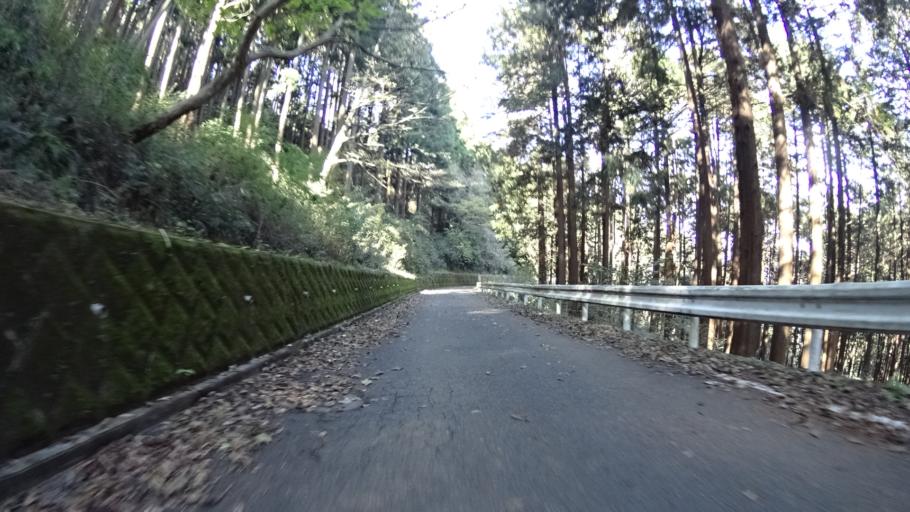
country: JP
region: Kanagawa
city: Atsugi
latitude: 35.5199
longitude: 139.2751
